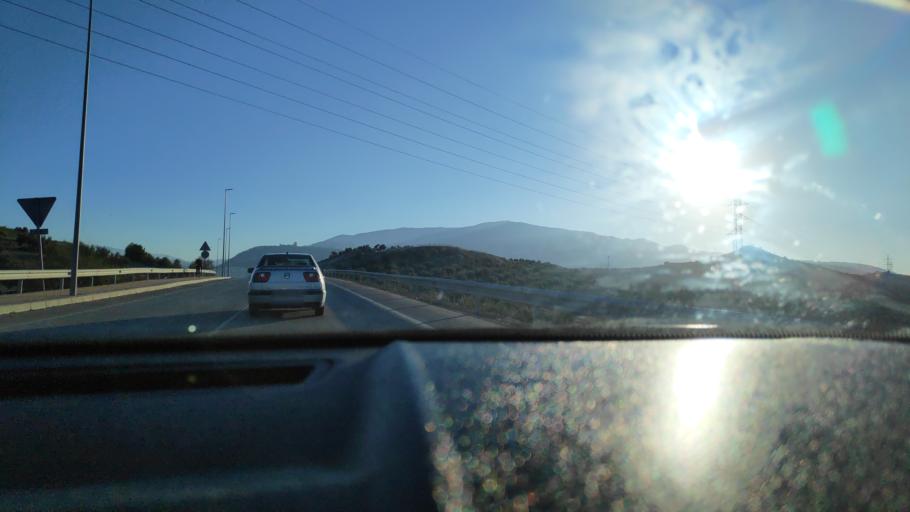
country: ES
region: Andalusia
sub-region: Provincia de Jaen
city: Jaen
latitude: 37.8079
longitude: -3.7877
